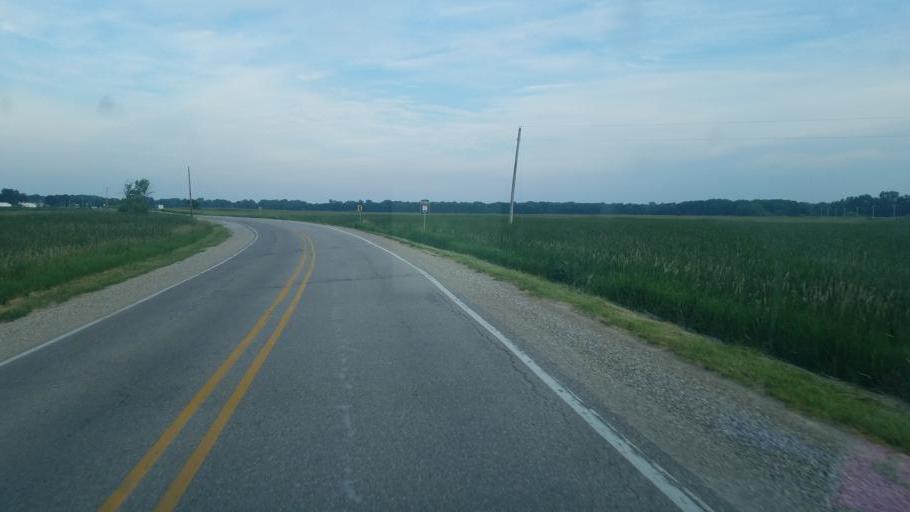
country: US
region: Iowa
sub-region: Benton County
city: Belle Plaine
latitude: 41.9424
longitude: -92.4150
